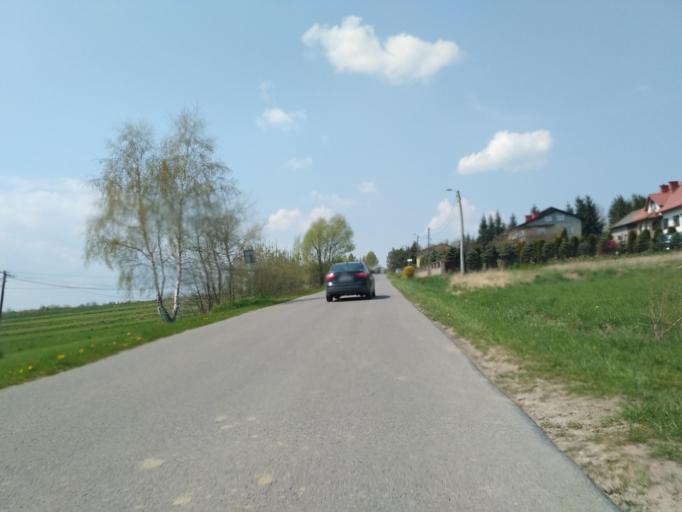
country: PL
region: Subcarpathian Voivodeship
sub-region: Powiat jasielski
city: Tarnowiec
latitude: 49.6708
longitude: 21.5534
